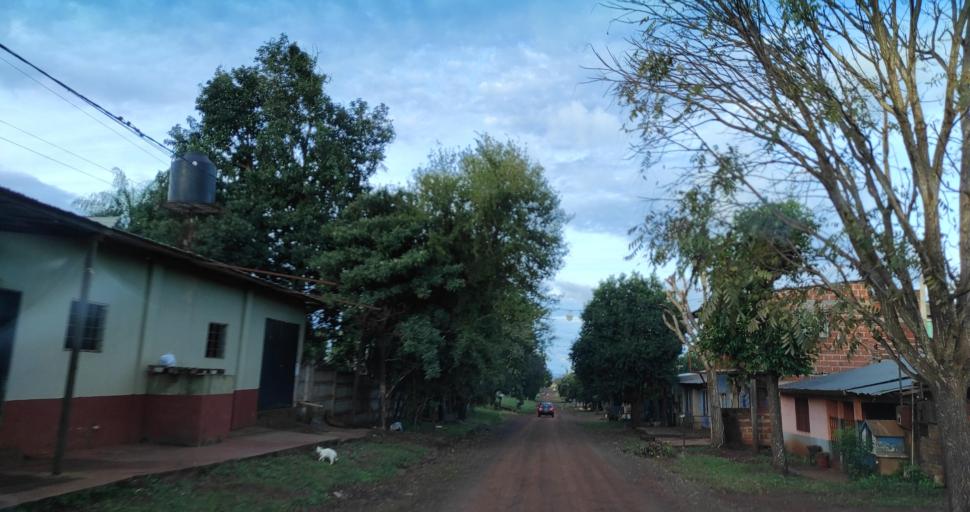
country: AR
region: Misiones
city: Garupa
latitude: -27.4818
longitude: -55.8605
